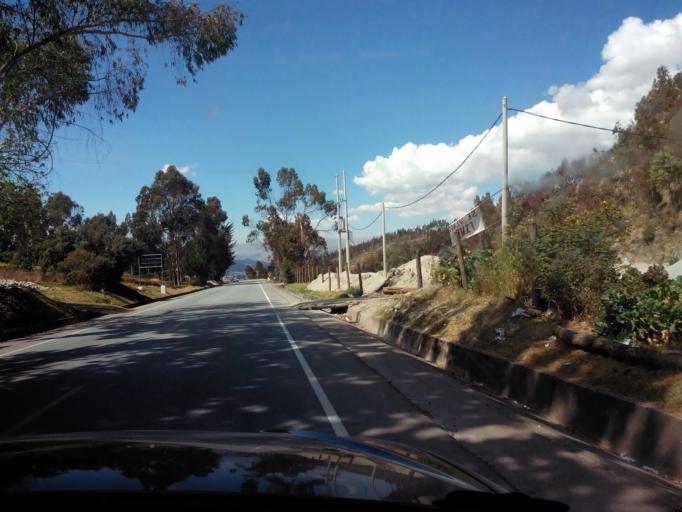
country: PE
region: Cusco
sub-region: Provincia de Anta
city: Ancahuasi
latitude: -13.4430
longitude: -72.3497
